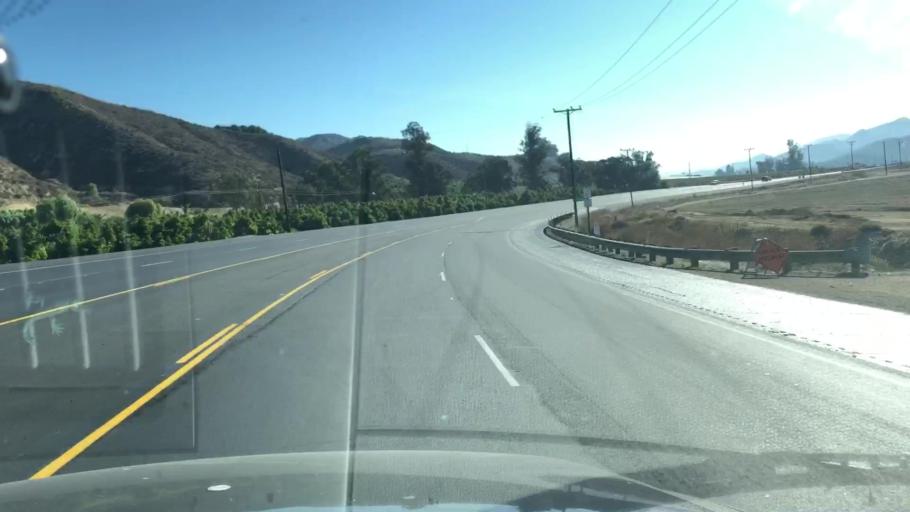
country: US
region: California
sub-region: Ventura County
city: Piru
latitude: 34.4110
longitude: -118.7833
